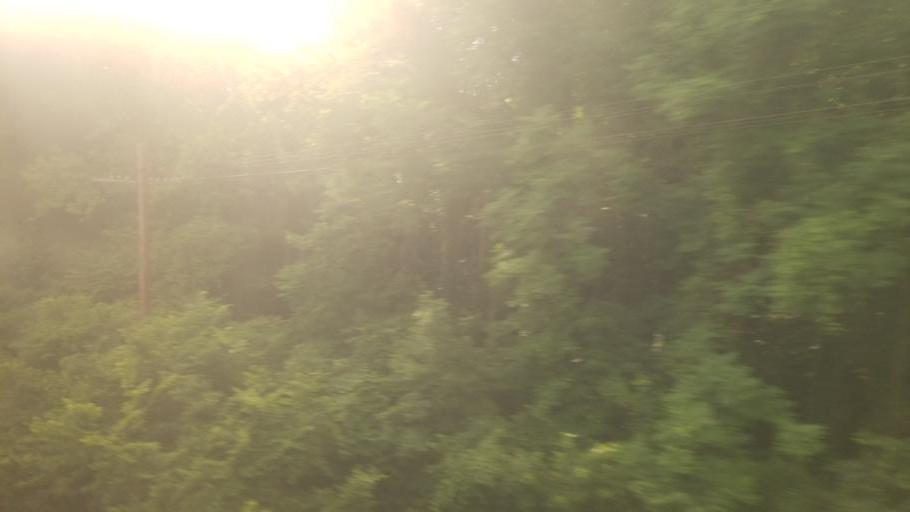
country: US
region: Kansas
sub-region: Douglas County
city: Eudora
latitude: 38.9513
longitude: -95.0891
